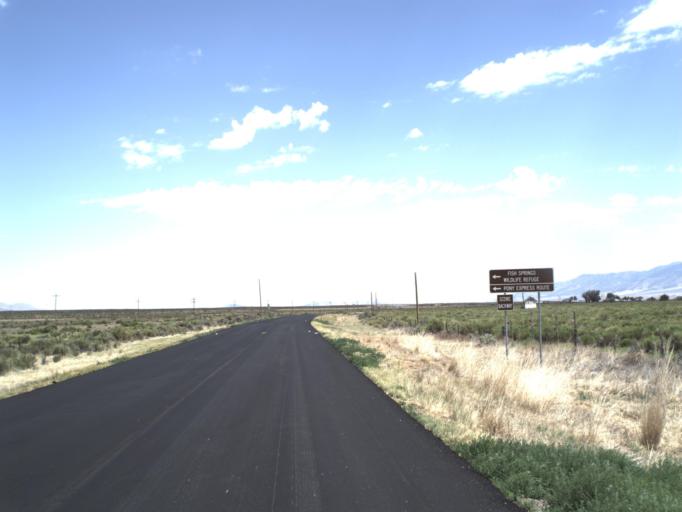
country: US
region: Utah
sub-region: Tooele County
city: Tooele
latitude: 40.1605
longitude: -112.4307
